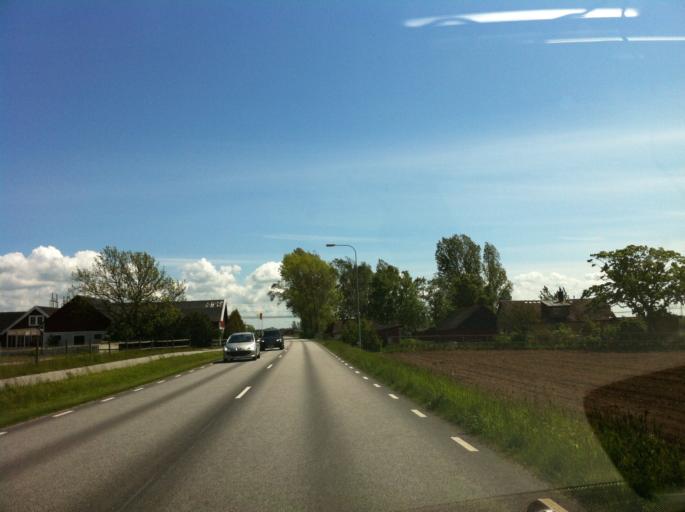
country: SE
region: Skane
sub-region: Kavlinge Kommun
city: Loddekopinge
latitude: 55.7905
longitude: 12.9991
